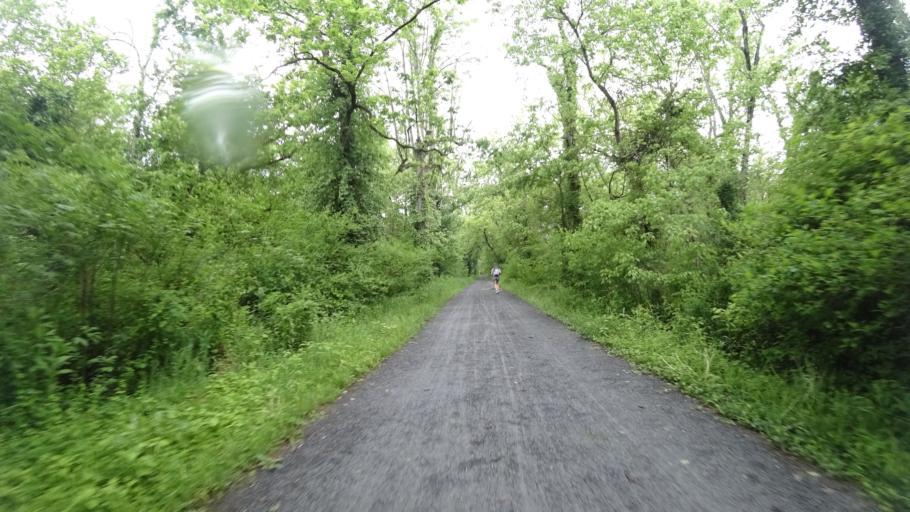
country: US
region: Maryland
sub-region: Frederick County
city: Brunswick
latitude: 39.3126
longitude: -77.6355
